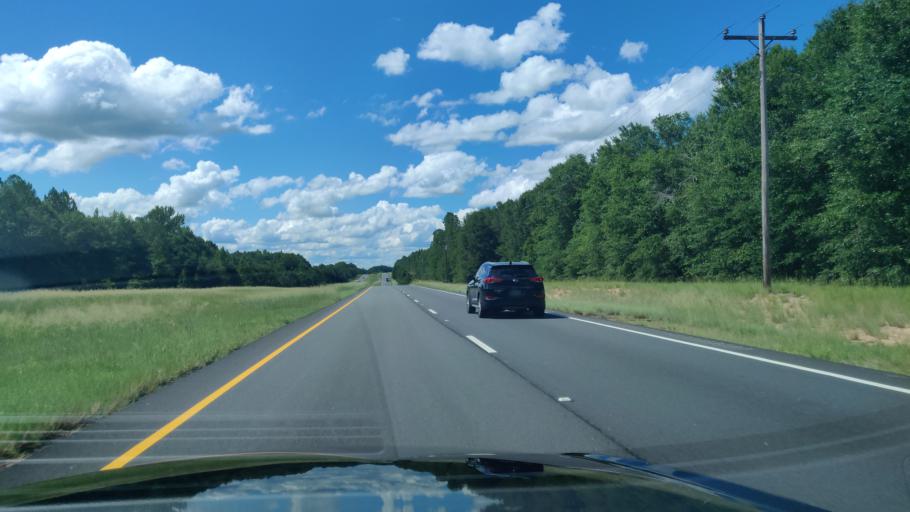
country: US
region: Georgia
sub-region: Chattahoochee County
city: Cusseta
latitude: 32.2051
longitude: -84.7038
